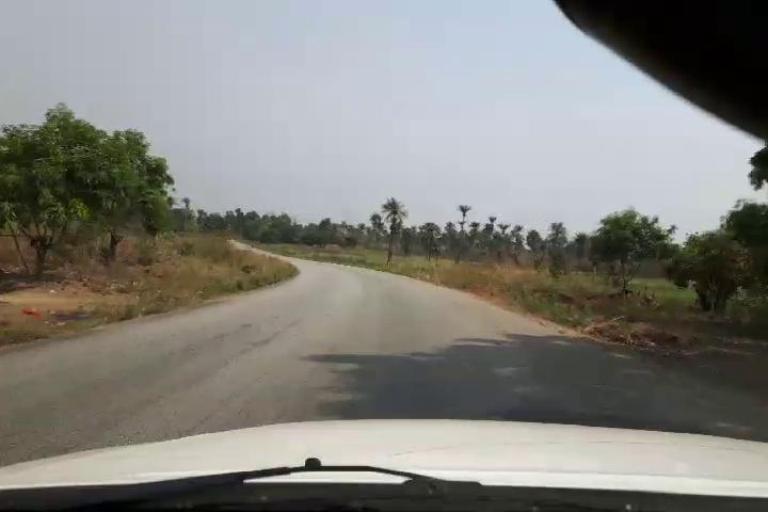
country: SL
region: Southern Province
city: Largo
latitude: 8.3102
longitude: -12.2147
